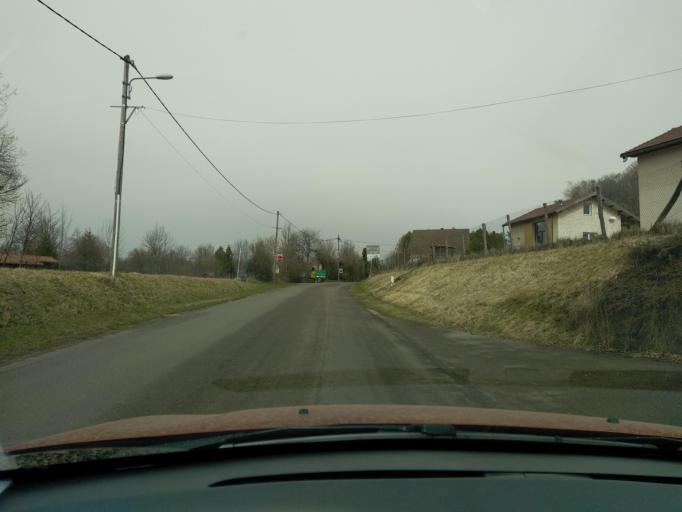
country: FR
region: Franche-Comte
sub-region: Departement du Jura
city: Clairvaux-les-Lacs
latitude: 46.6500
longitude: 5.7749
